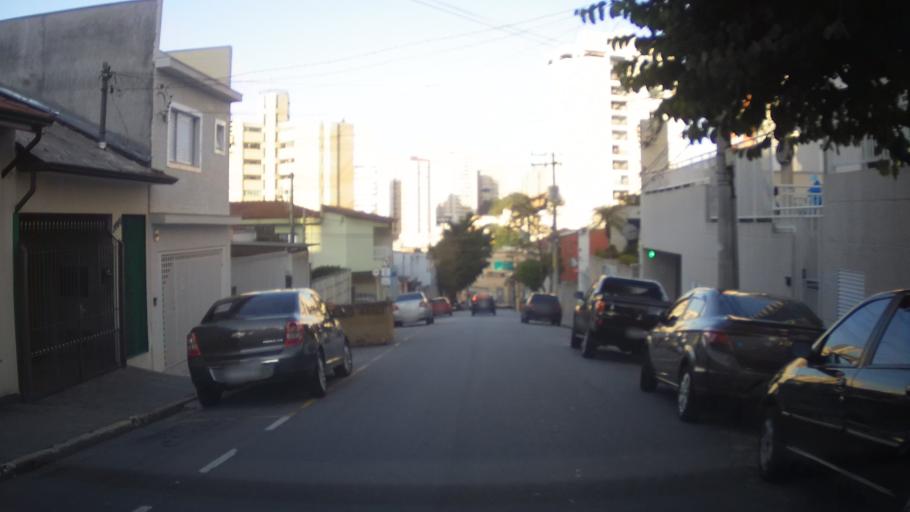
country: BR
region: Sao Paulo
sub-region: Sao Caetano Do Sul
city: Sao Caetano do Sul
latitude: -23.6210
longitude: -46.5592
